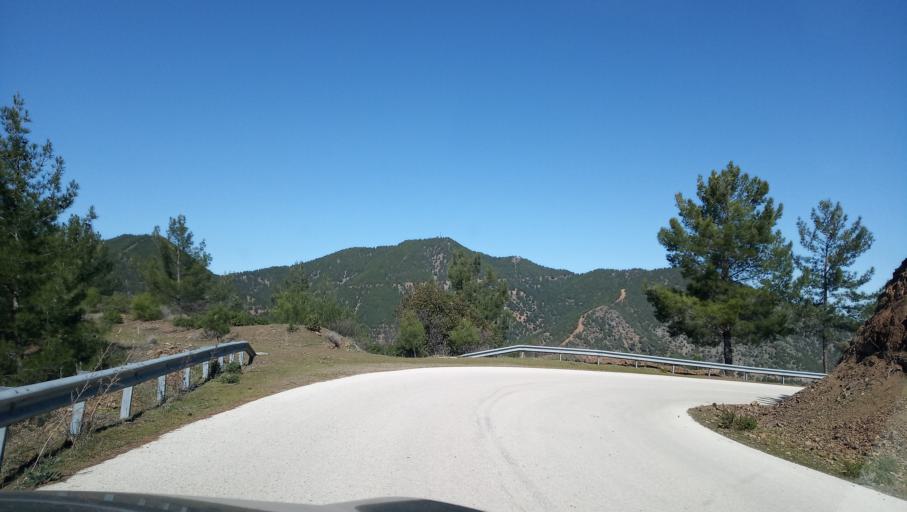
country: CY
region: Lefkosia
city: Lefka
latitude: 35.0645
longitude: 32.7435
